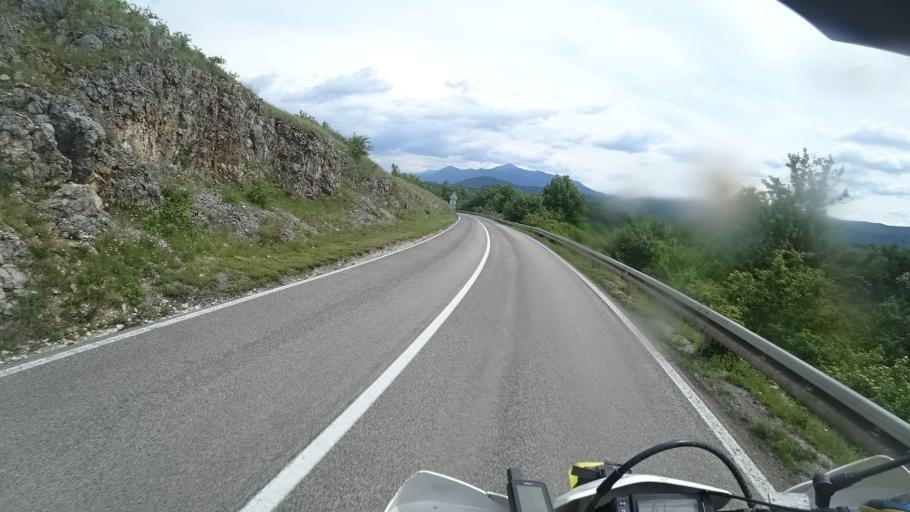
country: BA
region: Federation of Bosnia and Herzegovina
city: Izacic
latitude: 44.9218
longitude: 15.7046
